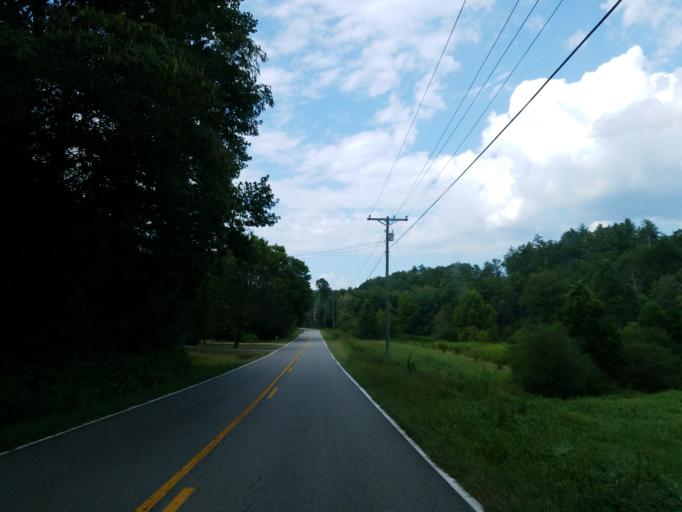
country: US
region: Georgia
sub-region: Gilmer County
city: Ellijay
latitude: 34.7620
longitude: -84.4226
